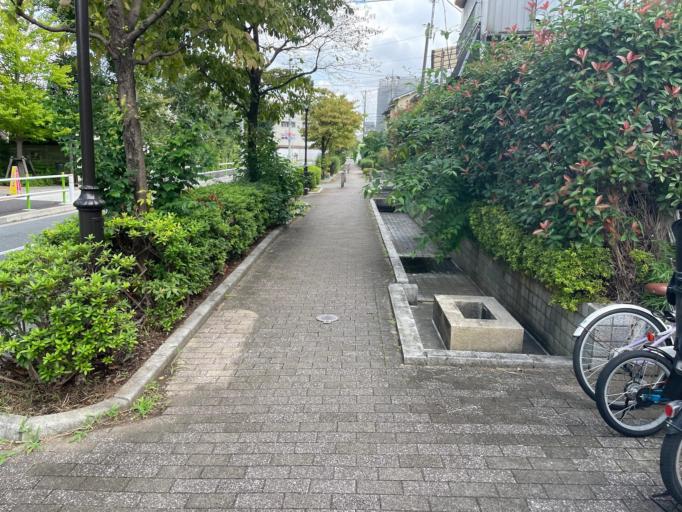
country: JP
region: Saitama
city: Wako
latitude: 35.7882
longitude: 139.6368
